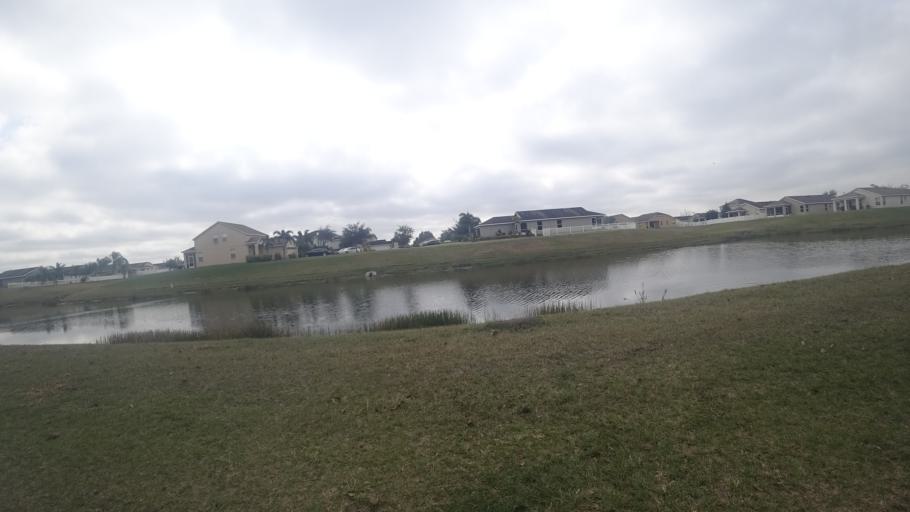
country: US
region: Florida
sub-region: Manatee County
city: Ellenton
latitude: 27.5795
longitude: -82.5100
